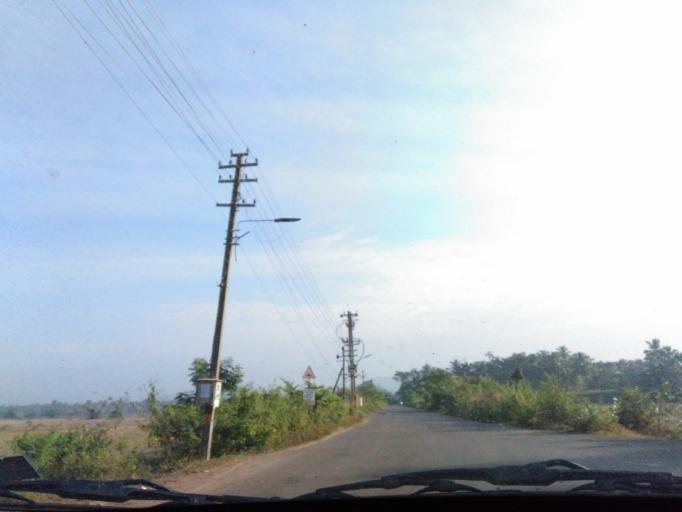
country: IN
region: Goa
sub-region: South Goa
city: Chinchinim
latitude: 15.2140
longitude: 73.9721
